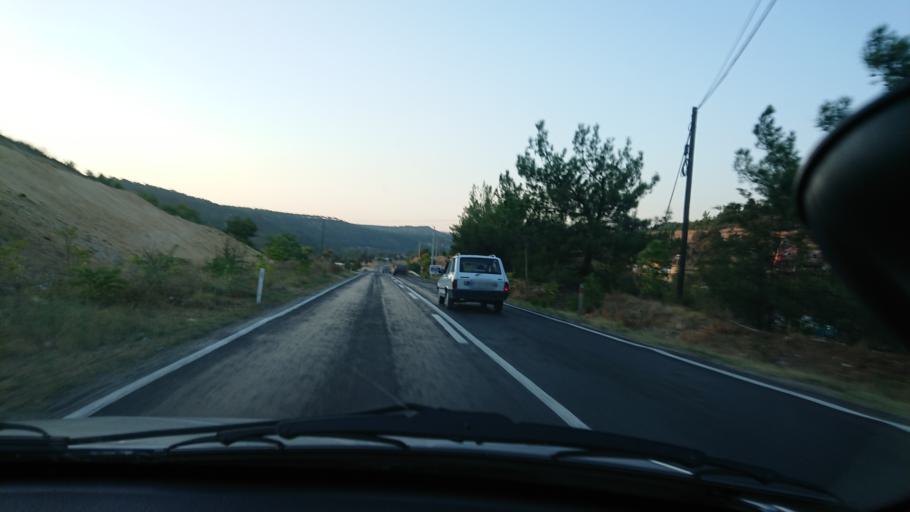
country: TR
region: Usak
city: Gure
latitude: 38.7435
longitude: 29.2009
